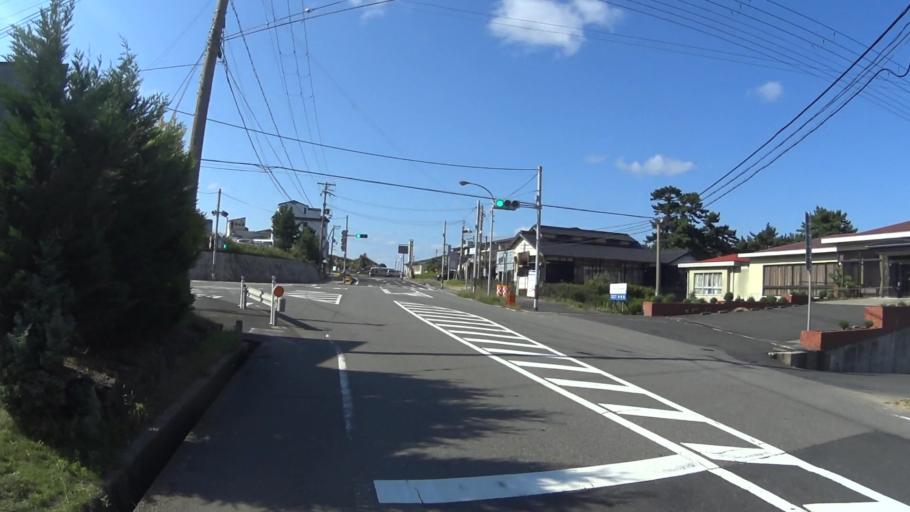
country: JP
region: Kyoto
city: Miyazu
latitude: 35.7396
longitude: 135.1032
